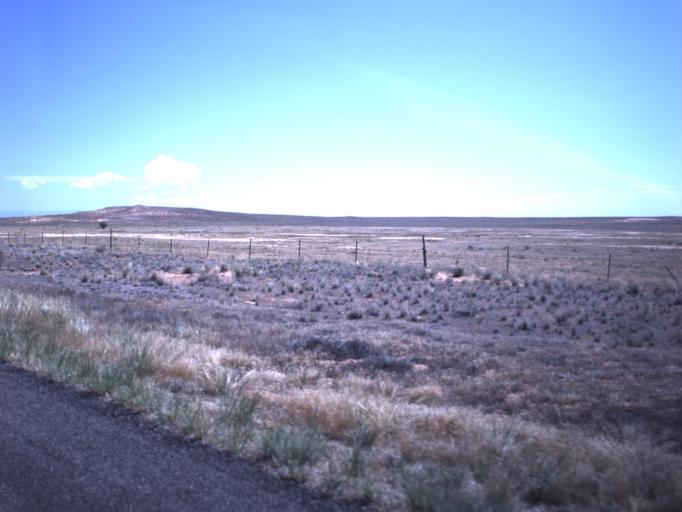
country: US
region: Utah
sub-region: Emery County
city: Ferron
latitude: 38.6345
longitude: -110.5642
